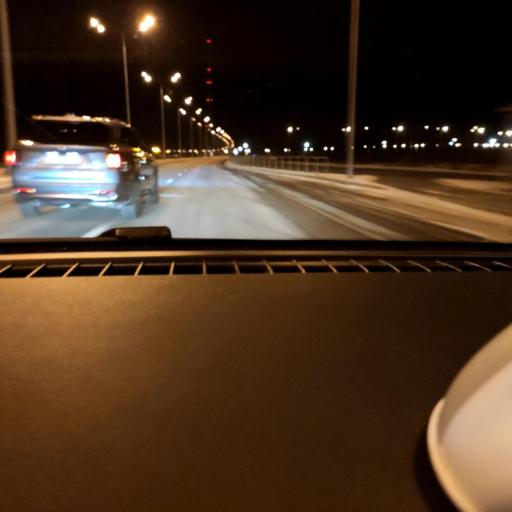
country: RU
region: Samara
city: Samara
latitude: 53.2855
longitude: 50.2355
